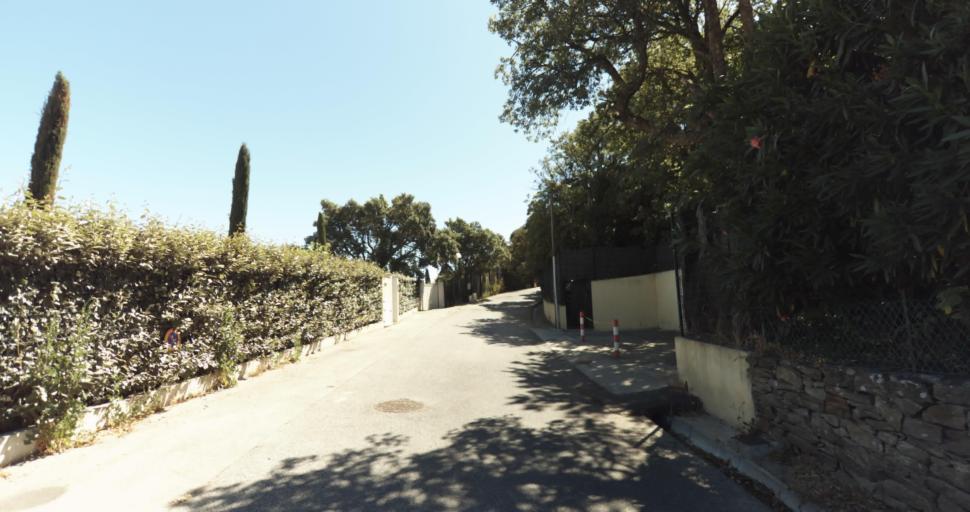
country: FR
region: Provence-Alpes-Cote d'Azur
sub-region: Departement du Var
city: Saint-Tropez
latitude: 43.2591
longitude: 6.6080
